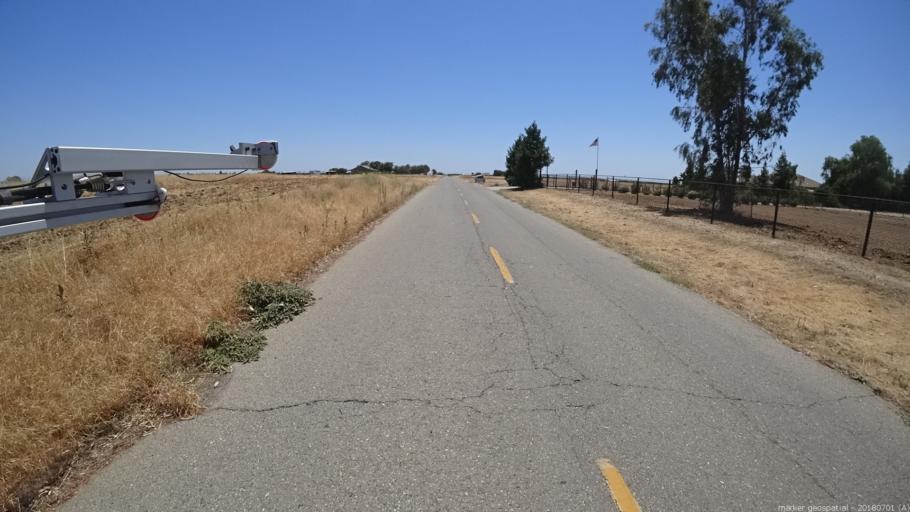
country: US
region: California
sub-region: Madera County
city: Madera Acres
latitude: 37.0663
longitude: -120.0112
